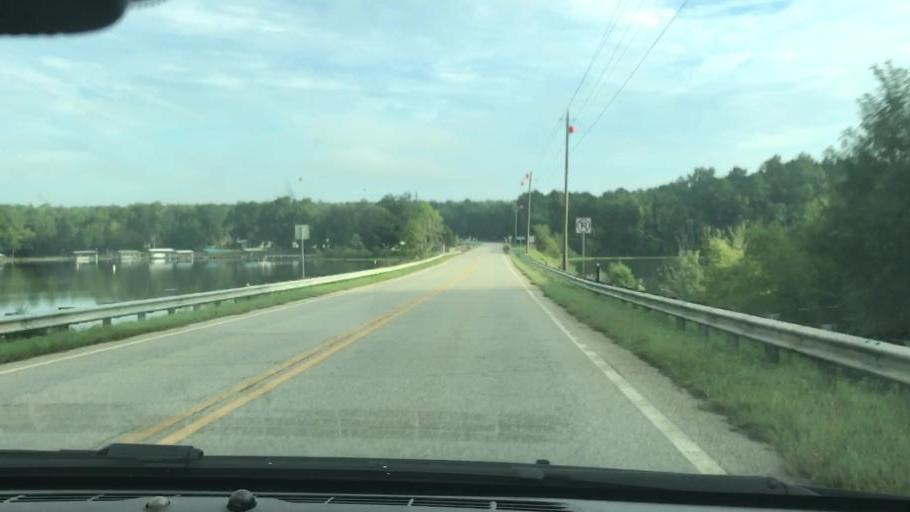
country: US
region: Georgia
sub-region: Clay County
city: Fort Gaines
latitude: 31.7459
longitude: -85.0544
